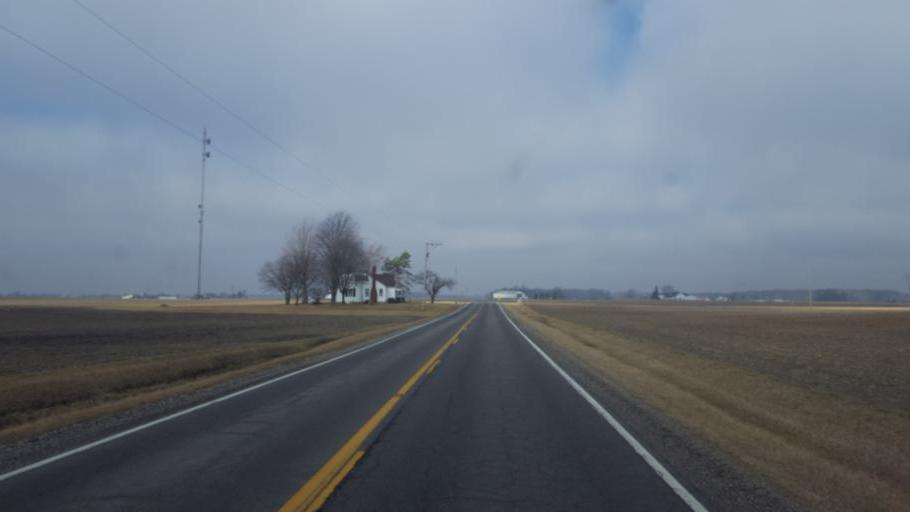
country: US
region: Ohio
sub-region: Crawford County
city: Galion
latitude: 40.7147
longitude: -82.8799
